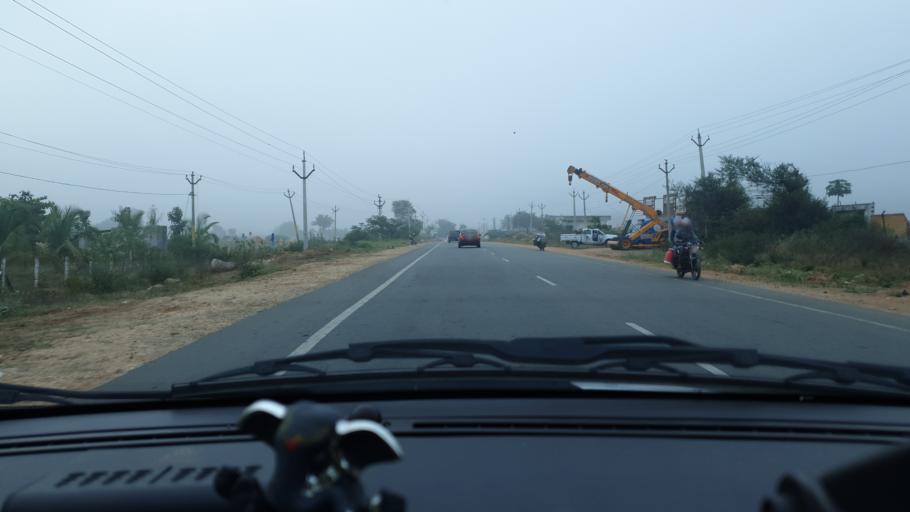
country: IN
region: Telangana
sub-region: Mahbubnagar
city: Farrukhnagar
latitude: 16.9286
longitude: 78.5278
